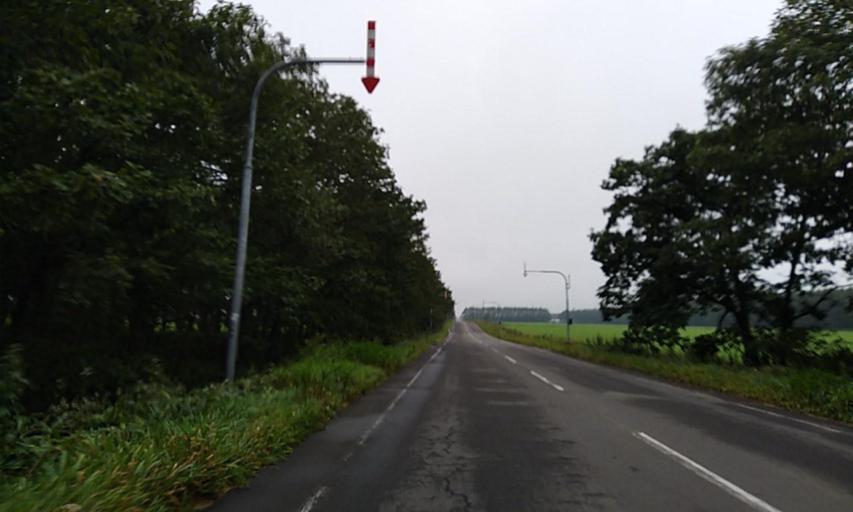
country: JP
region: Hokkaido
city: Shibetsu
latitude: 43.5184
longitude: 144.6820
